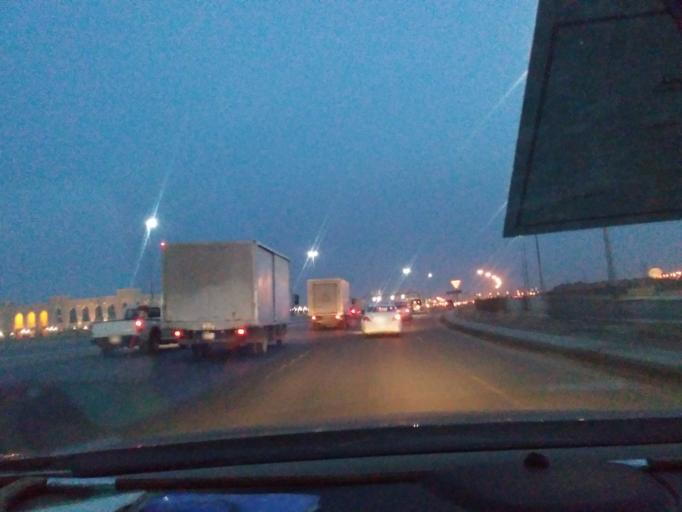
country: SA
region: Ar Riyad
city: Riyadh
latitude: 24.7610
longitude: 46.8436
